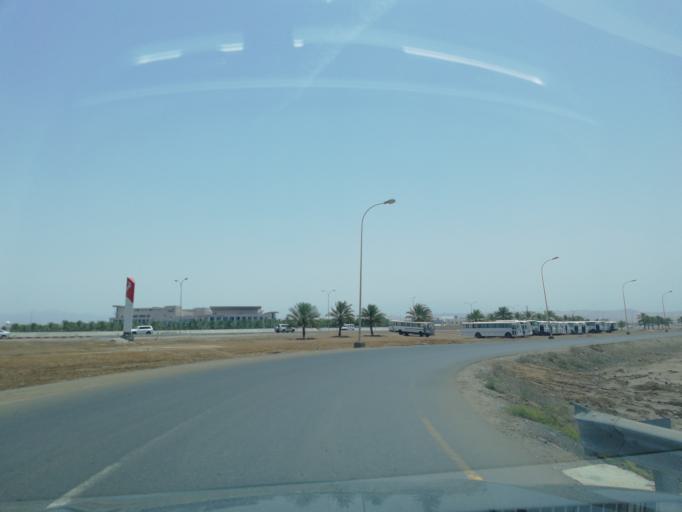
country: OM
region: Muhafazat Masqat
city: As Sib al Jadidah
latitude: 23.6249
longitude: 58.2629
